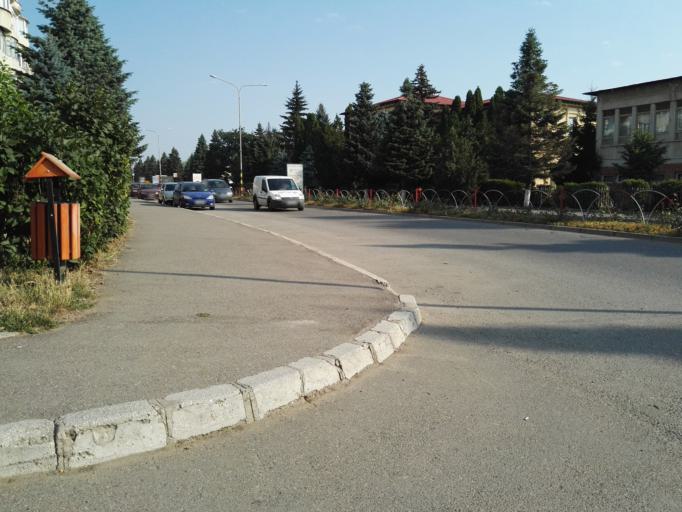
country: RO
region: Suceava
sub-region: Municipiul Falticeni
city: Falticeni
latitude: 47.4623
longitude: 26.3021
